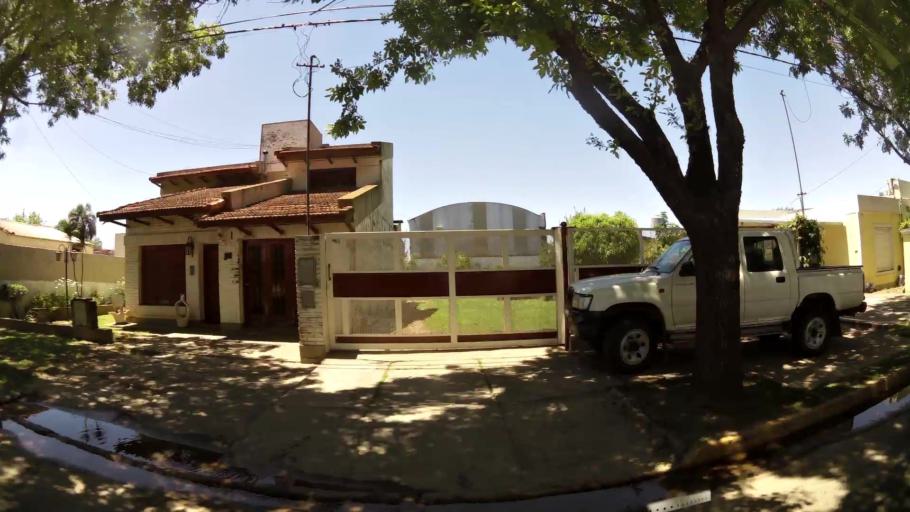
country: AR
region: Santa Fe
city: Rafaela
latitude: -31.2484
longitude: -61.4625
